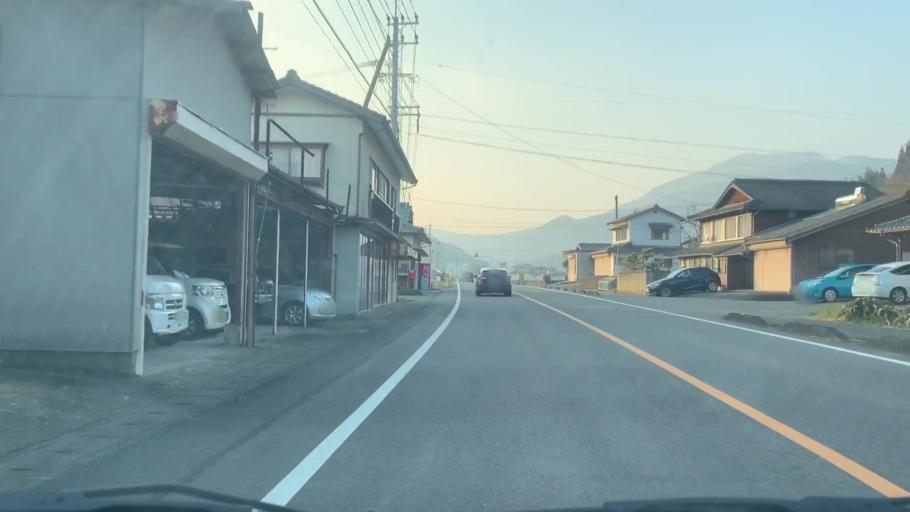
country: JP
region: Saga Prefecture
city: Takeocho-takeo
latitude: 33.2593
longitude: 130.0661
